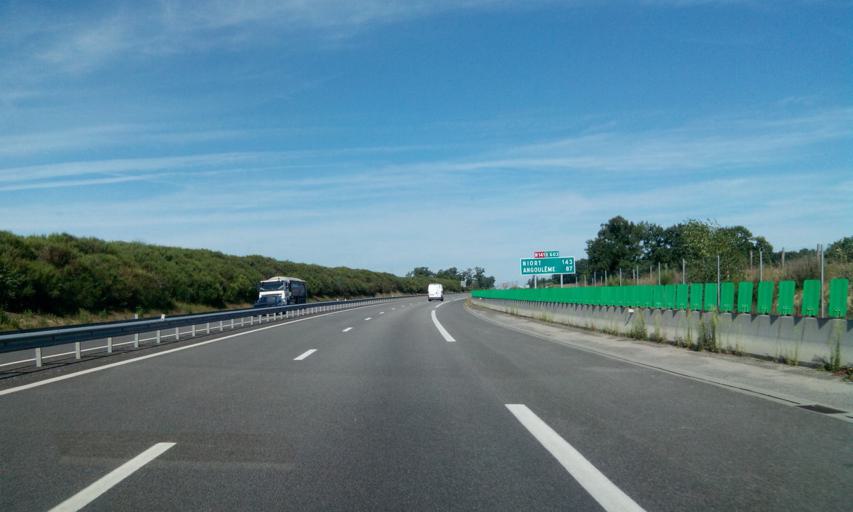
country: FR
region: Limousin
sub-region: Departement de la Haute-Vienne
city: Veyrac
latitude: 45.8833
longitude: 1.0869
